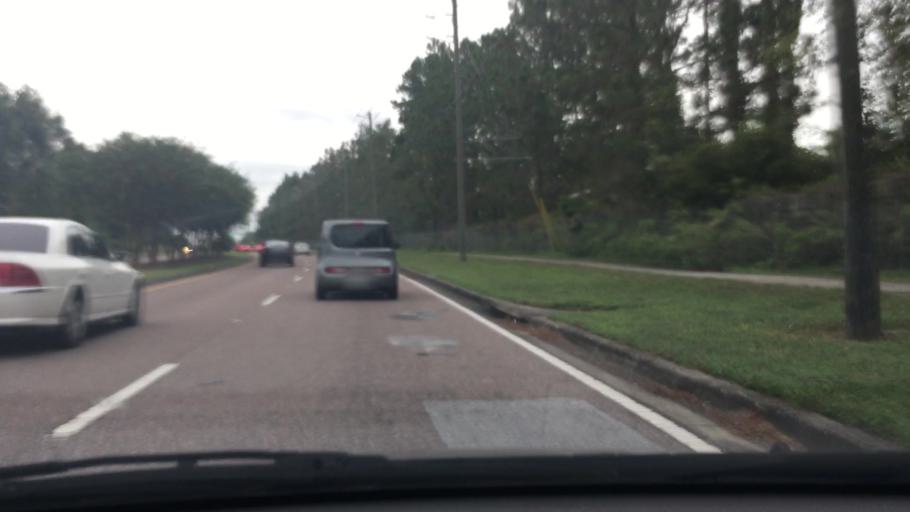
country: US
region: Florida
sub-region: Pasco County
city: Land O' Lakes
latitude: 28.1946
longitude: -82.4345
